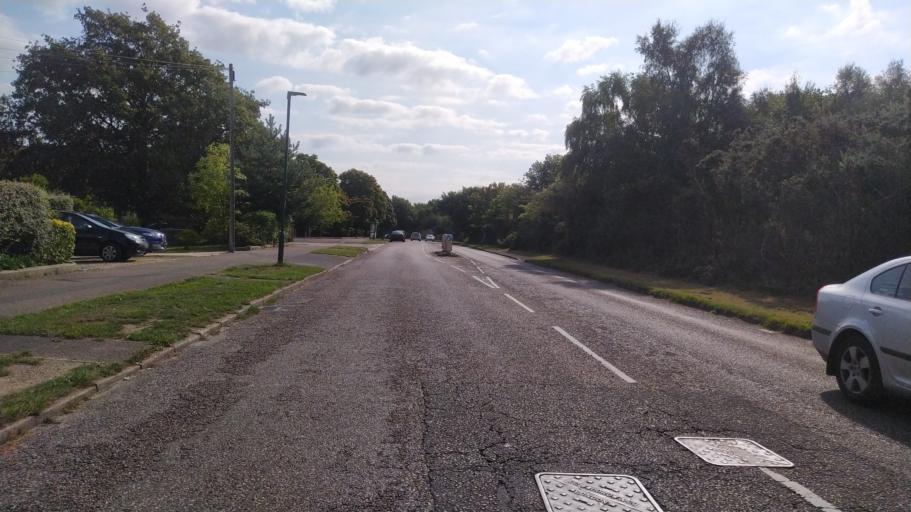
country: GB
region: England
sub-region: Dorset
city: Parkstone
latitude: 50.7535
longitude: -1.9140
